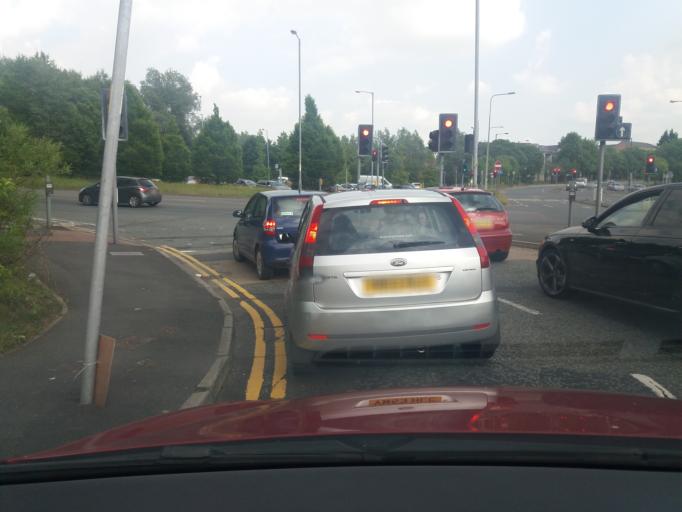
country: GB
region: England
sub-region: Borough of Bolton
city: Horwich
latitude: 53.5818
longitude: -2.5278
